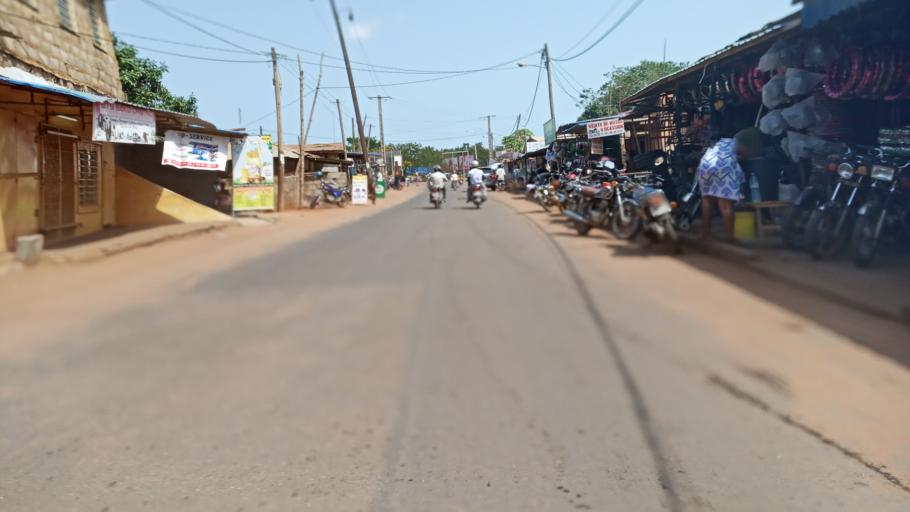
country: TG
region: Maritime
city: Lome
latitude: 6.2226
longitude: 1.2084
